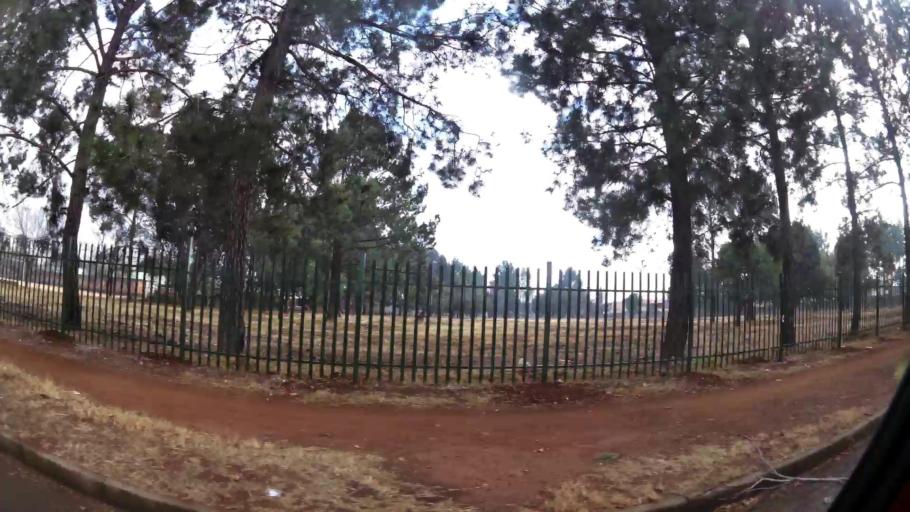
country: ZA
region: Gauteng
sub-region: Sedibeng District Municipality
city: Vanderbijlpark
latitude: -26.7008
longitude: 27.8283
